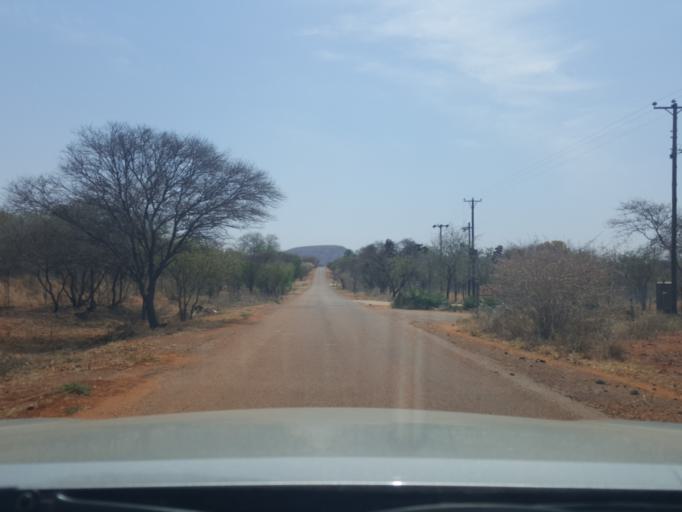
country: BW
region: South East
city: Ramotswa
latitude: -24.7706
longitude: 25.8452
